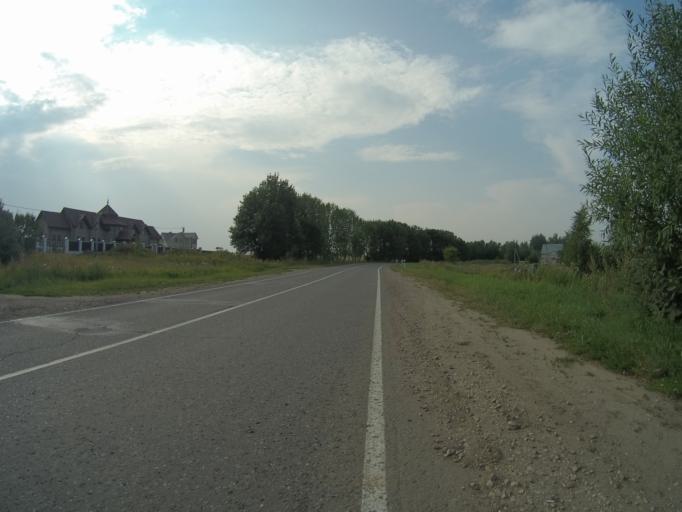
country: RU
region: Vladimir
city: Suzdal'
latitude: 56.4124
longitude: 40.4296
